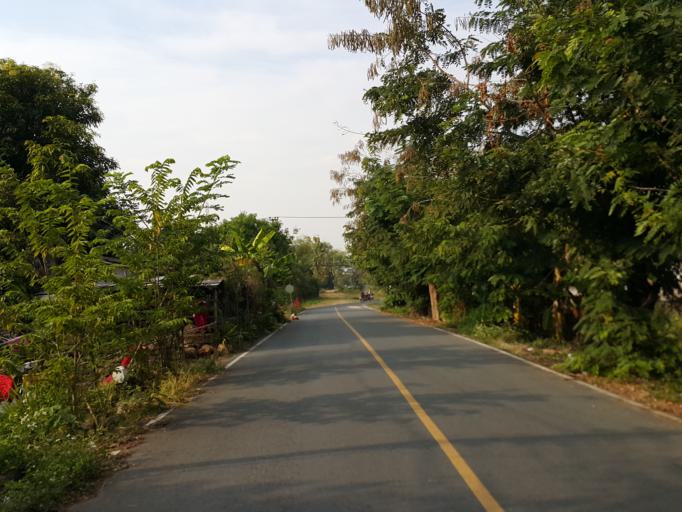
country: TH
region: Chiang Mai
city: San Sai
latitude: 18.8685
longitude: 99.1382
